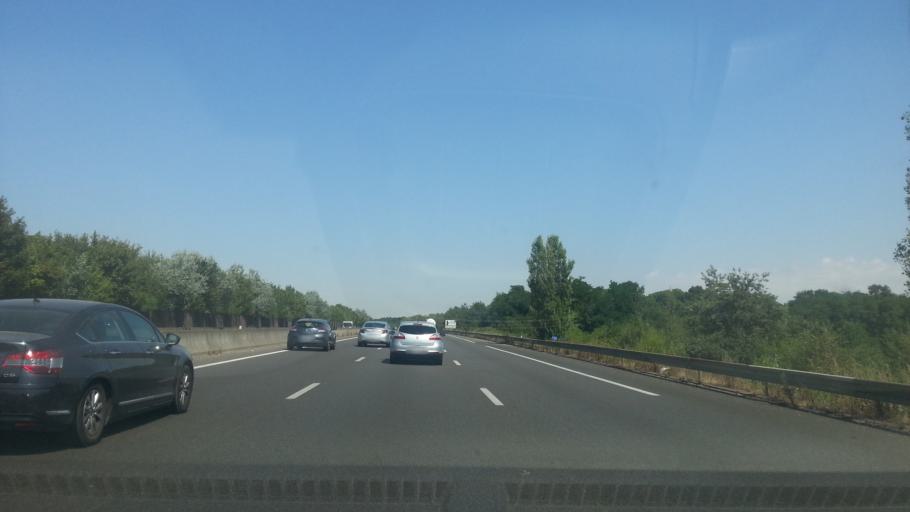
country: FR
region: Centre
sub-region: Departement du Loiret
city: Saint-Jean-de-la-Ruelle
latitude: 47.9243
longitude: 1.8491
